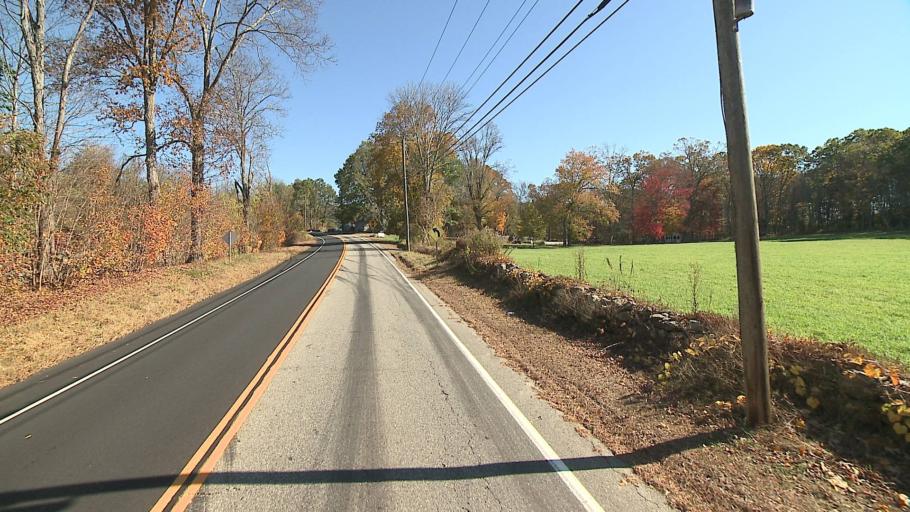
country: US
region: Connecticut
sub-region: Tolland County
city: South Coventry
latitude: 41.8015
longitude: -72.3058
